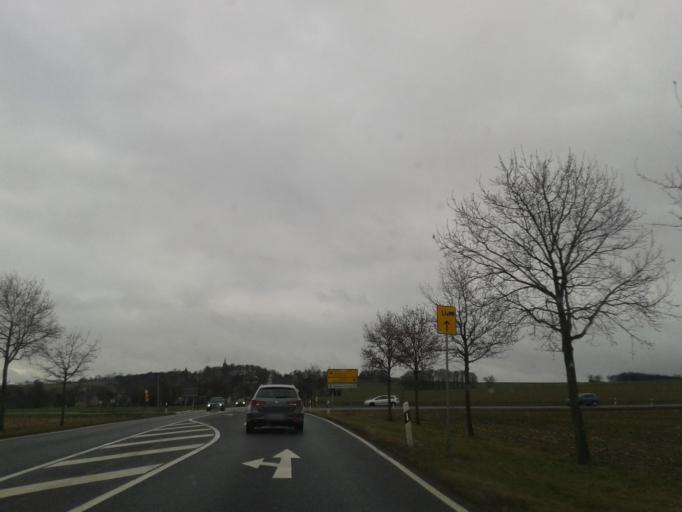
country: DE
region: Saxony
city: Durrhennersdorf
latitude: 51.0447
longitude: 14.6345
